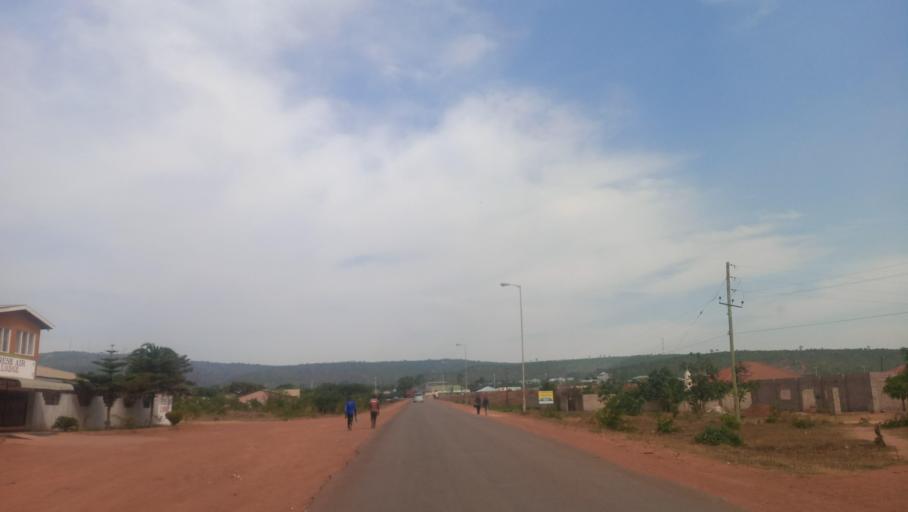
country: ZM
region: Northern
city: Mpika
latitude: -11.8420
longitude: 31.4401
